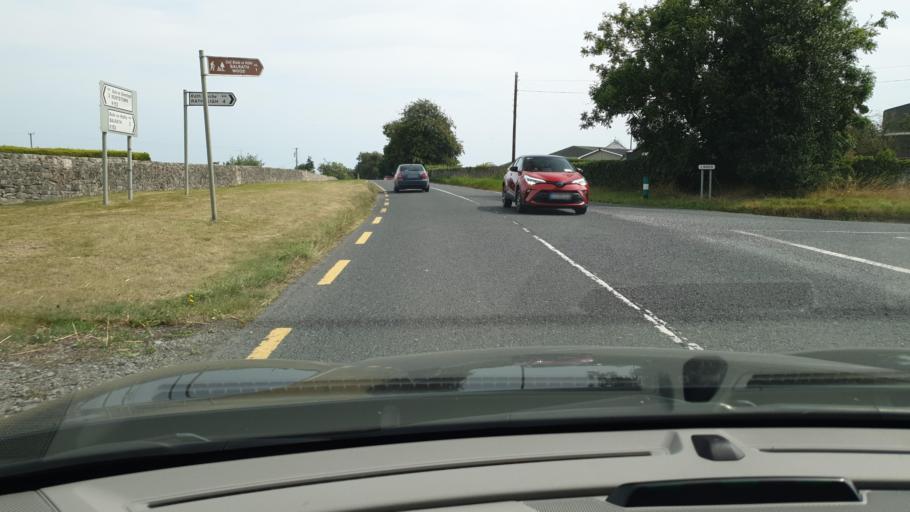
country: IE
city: Kentstown
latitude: 53.6221
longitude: -6.5111
